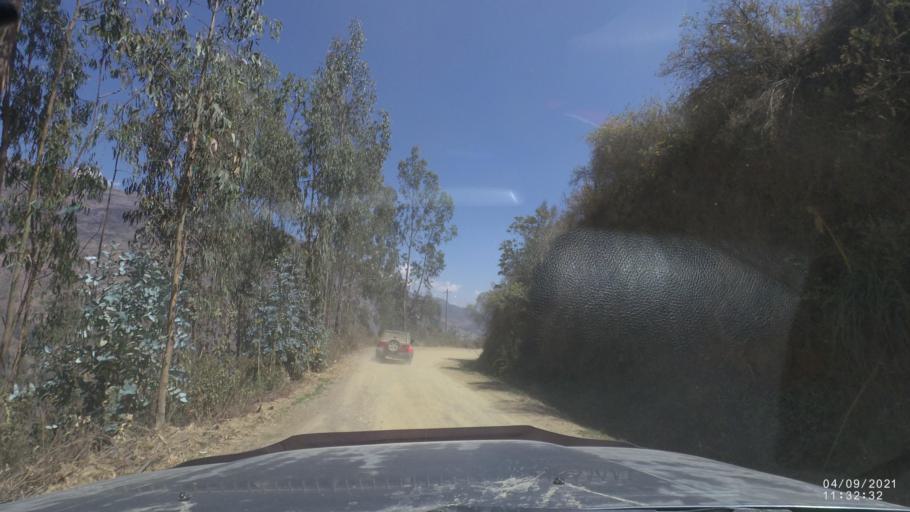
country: BO
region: Cochabamba
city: Colchani
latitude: -17.2292
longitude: -66.5221
